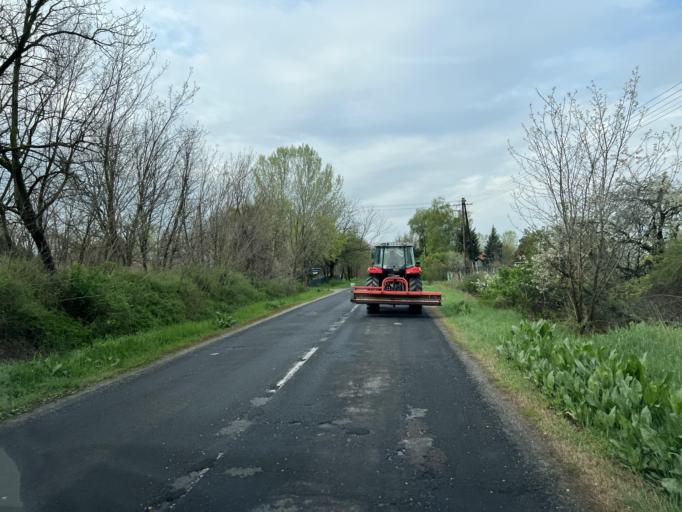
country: HU
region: Pest
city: Albertirsa
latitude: 47.2360
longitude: 19.5894
